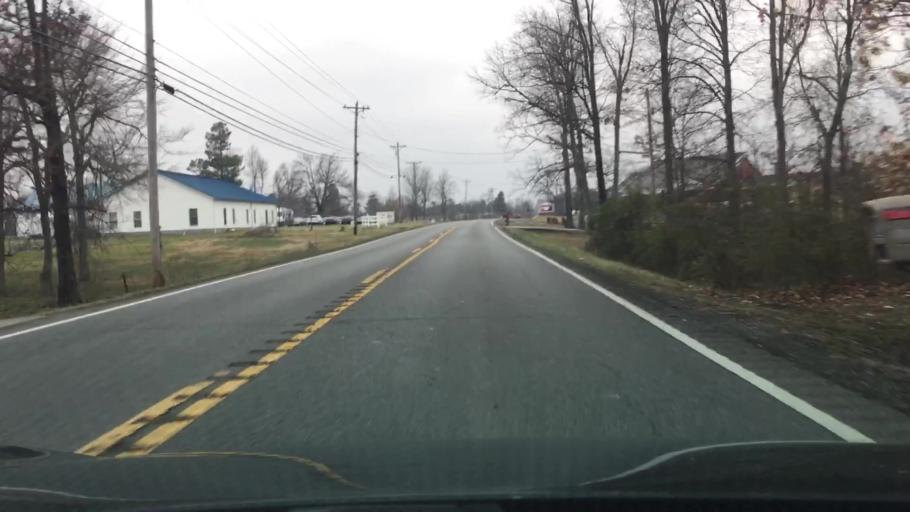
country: US
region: Kentucky
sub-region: Marshall County
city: Benton
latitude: 36.9412
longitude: -88.3611
